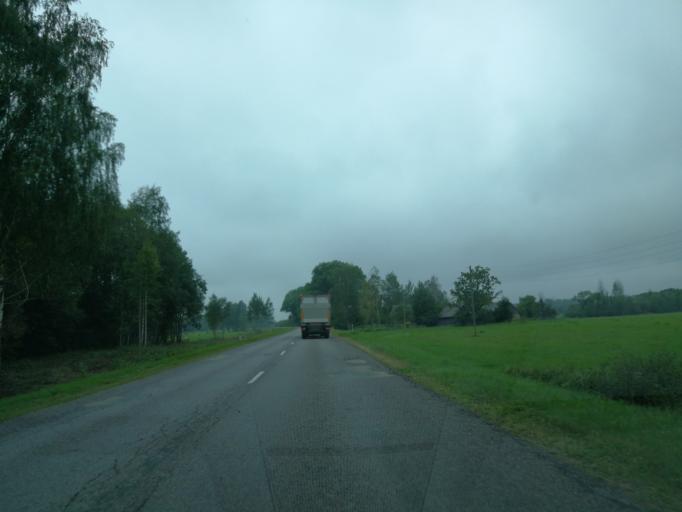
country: LV
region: Livani
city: Livani
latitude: 56.3469
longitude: 26.3175
